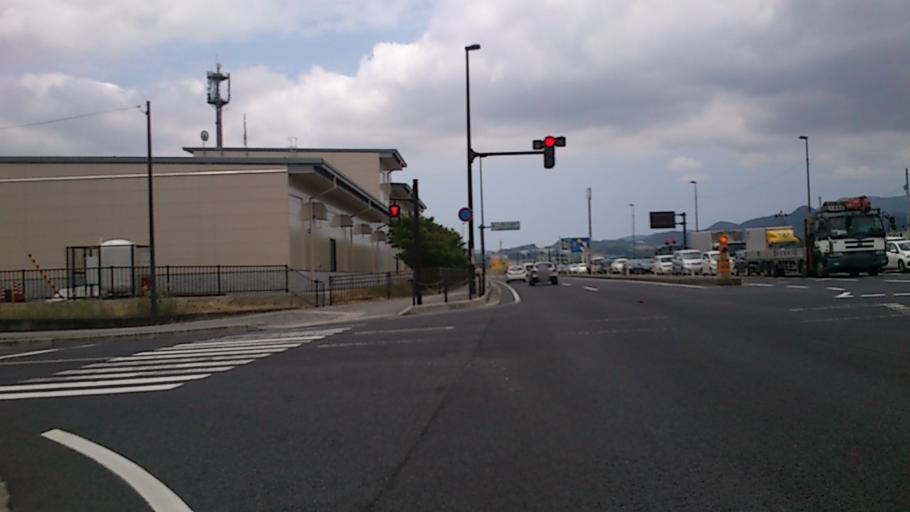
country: JP
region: Yamagata
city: Yamagata-shi
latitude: 38.2087
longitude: 140.3172
